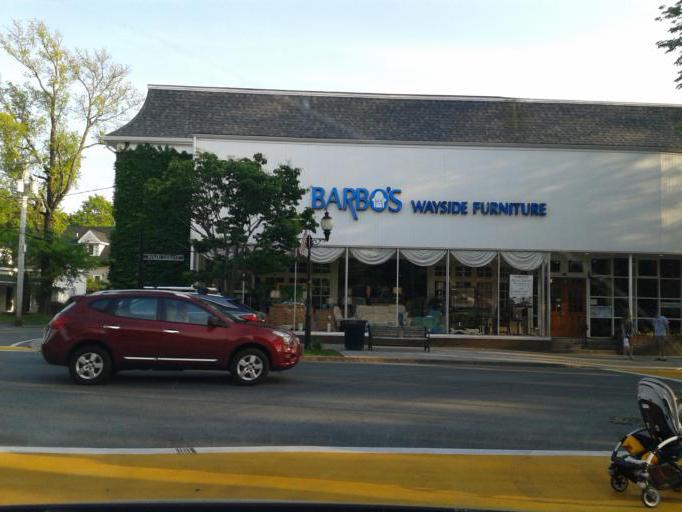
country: US
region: Massachusetts
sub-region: Barnstable County
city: Falmouth
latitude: 41.5523
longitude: -70.6131
